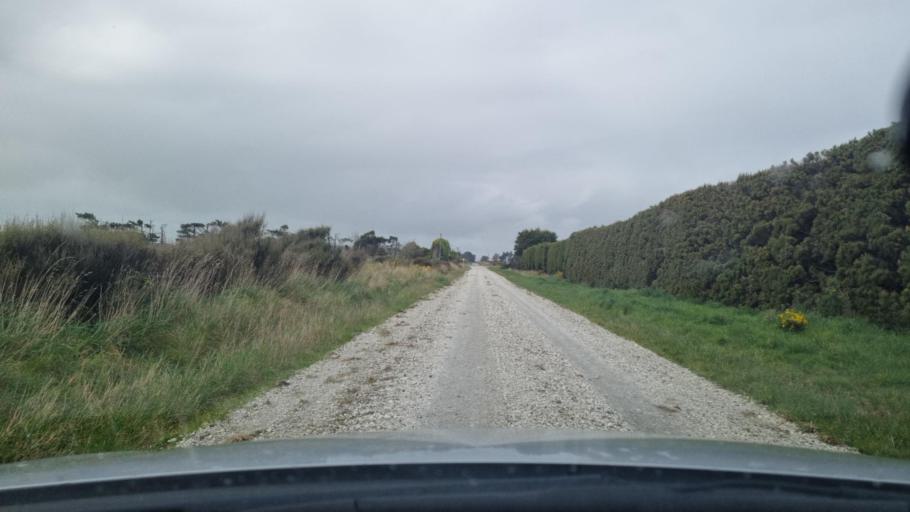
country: NZ
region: Southland
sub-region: Invercargill City
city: Invercargill
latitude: -46.4973
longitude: 168.4166
